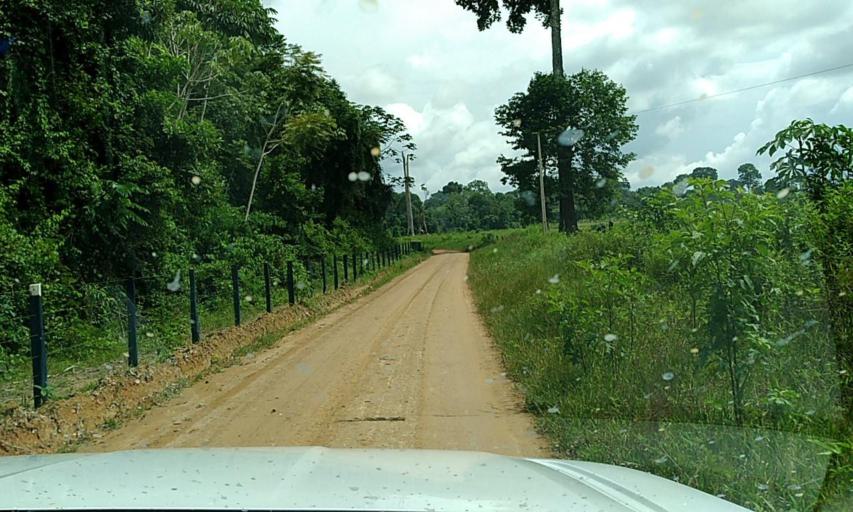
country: BR
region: Para
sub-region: Senador Jose Porfirio
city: Senador Jose Porfirio
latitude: -2.5184
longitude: -51.8381
